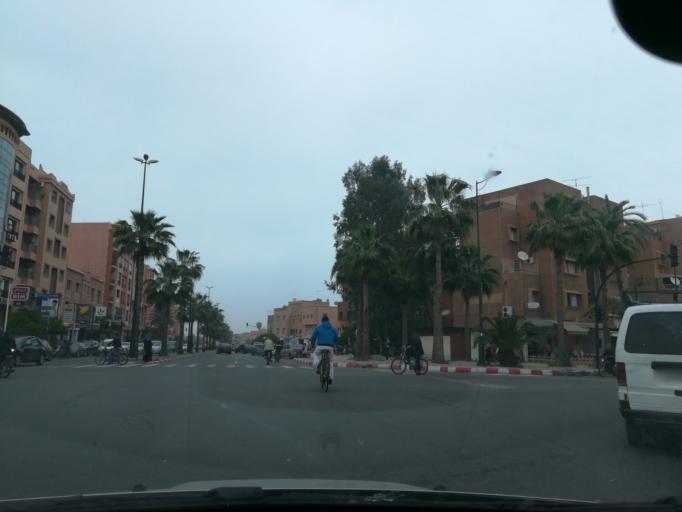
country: MA
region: Marrakech-Tensift-Al Haouz
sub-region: Marrakech
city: Marrakesh
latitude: 31.6477
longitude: -8.0007
